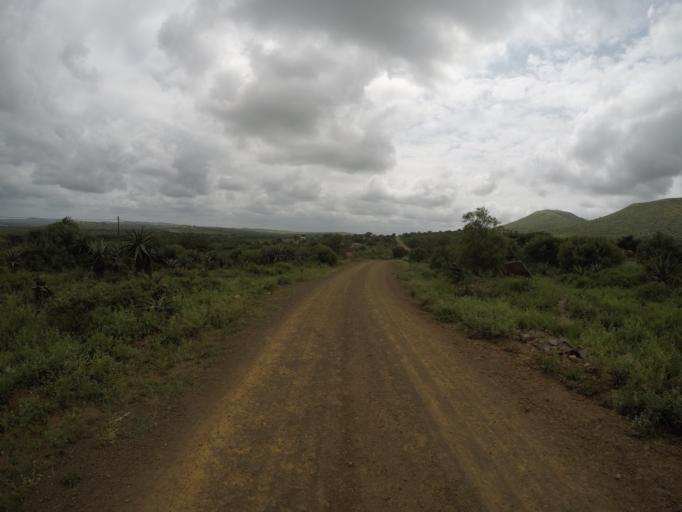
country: ZA
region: KwaZulu-Natal
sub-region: uThungulu District Municipality
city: Empangeni
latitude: -28.5829
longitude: 31.8651
